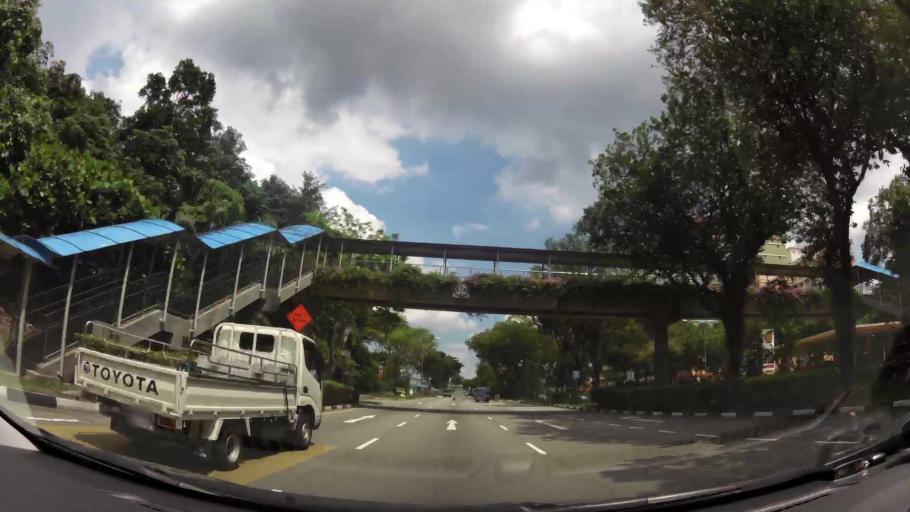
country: MY
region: Johor
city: Johor Bahru
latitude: 1.4447
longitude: 103.7896
